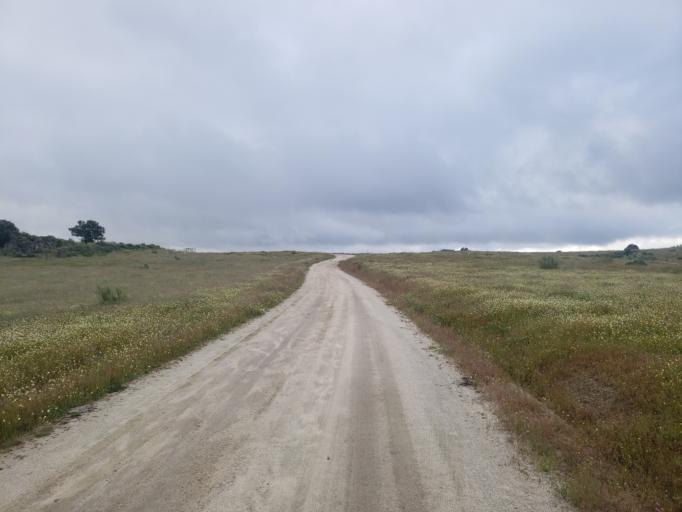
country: ES
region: Extremadura
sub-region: Provincia de Caceres
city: Malpartida de Caceres
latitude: 39.4279
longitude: -6.5040
